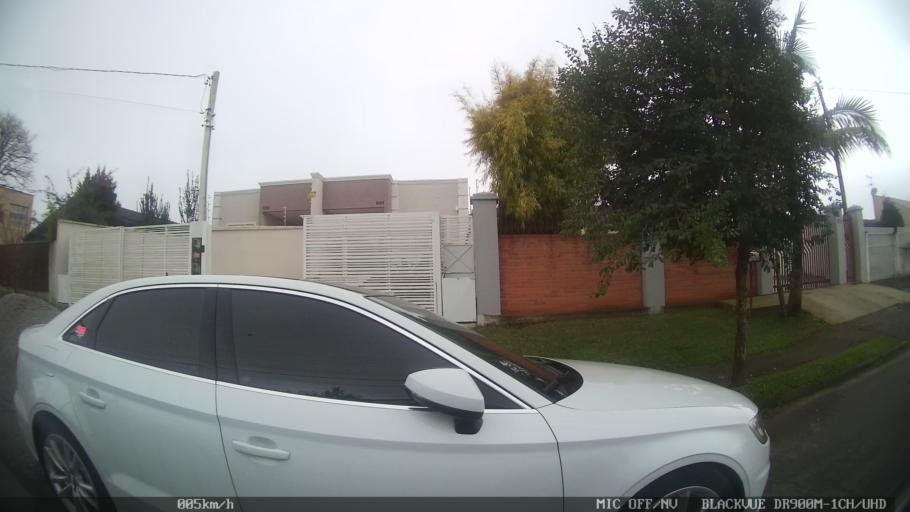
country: BR
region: Parana
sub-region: Sao Jose Dos Pinhais
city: Sao Jose dos Pinhais
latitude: -25.6068
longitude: -49.1669
